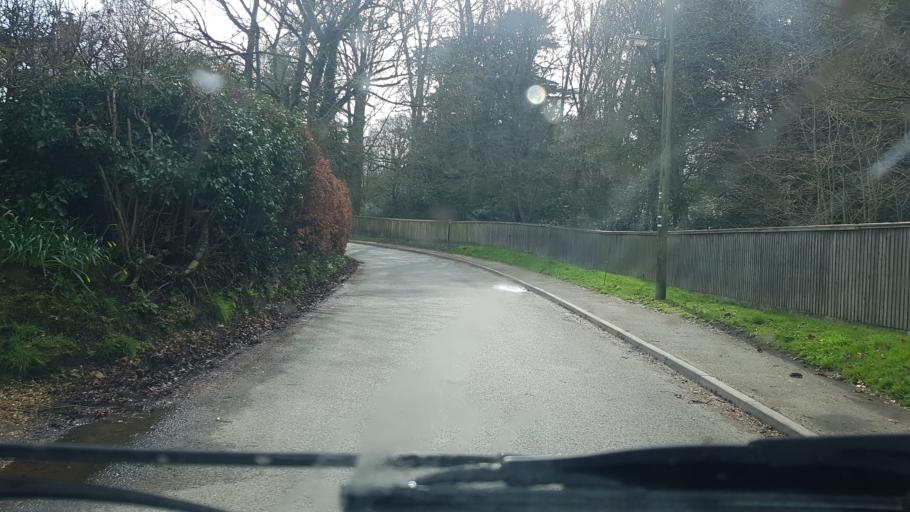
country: GB
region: England
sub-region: Wiltshire
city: Market Lavington
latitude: 51.3123
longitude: -1.9482
